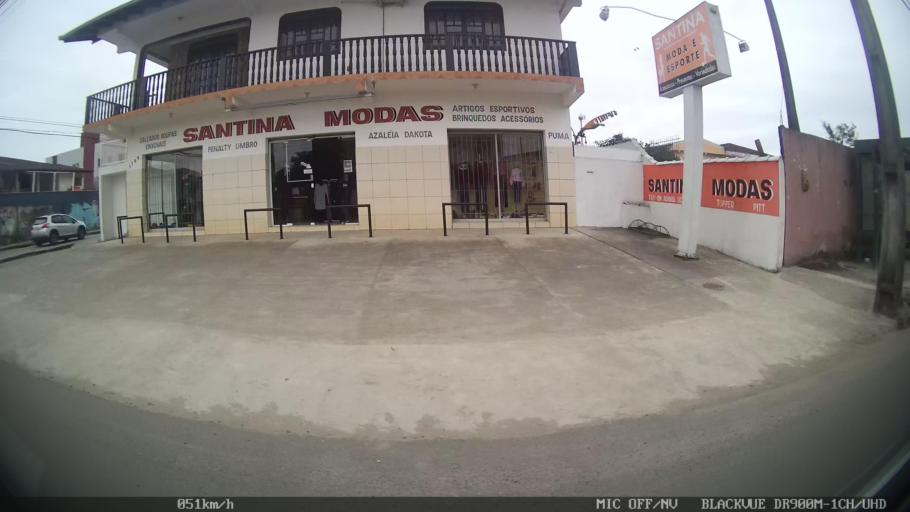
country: BR
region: Santa Catarina
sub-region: Joinville
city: Joinville
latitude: -26.3248
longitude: -48.8175
